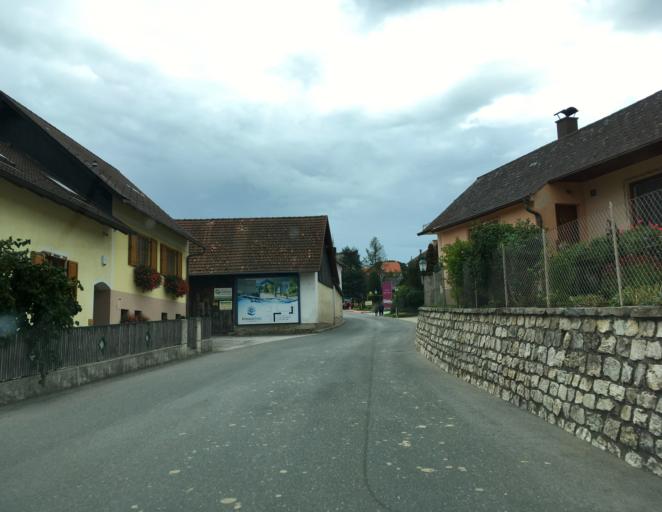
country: AT
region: Lower Austria
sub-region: Politischer Bezirk Wiener Neustadt
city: Bad Schonau
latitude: 47.4971
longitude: 16.2339
